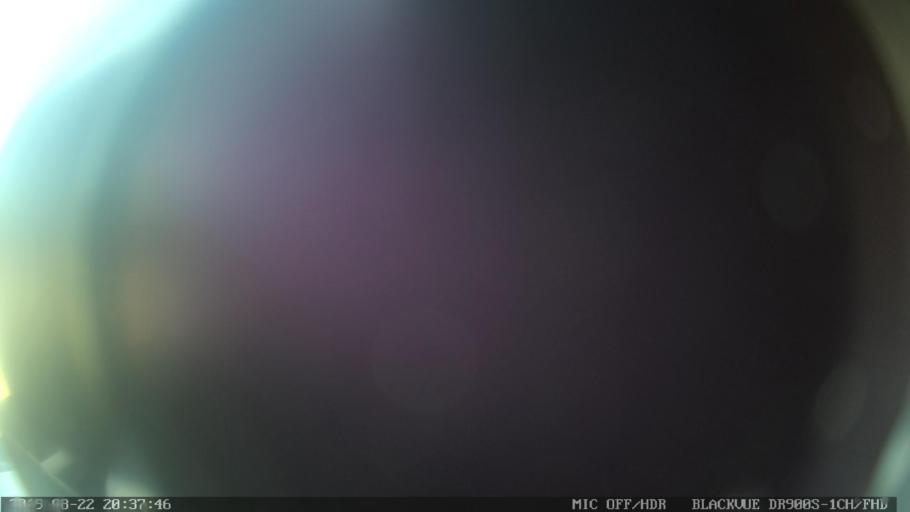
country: PT
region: Portalegre
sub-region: Nisa
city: Nisa
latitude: 39.6774
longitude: -7.7389
